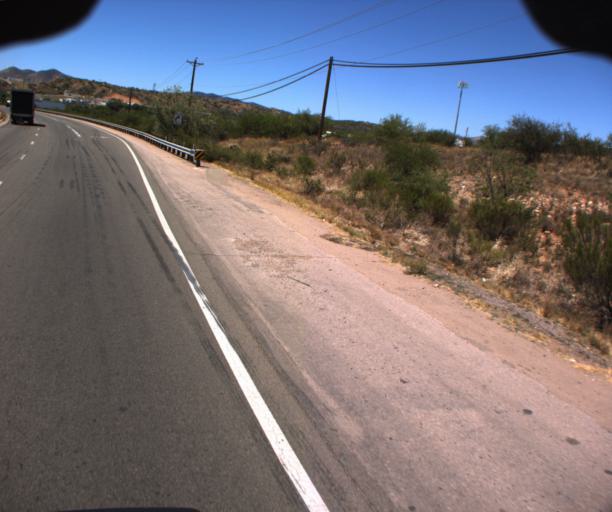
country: US
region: Arizona
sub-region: Santa Cruz County
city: Nogales
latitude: 31.3569
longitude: -110.9589
